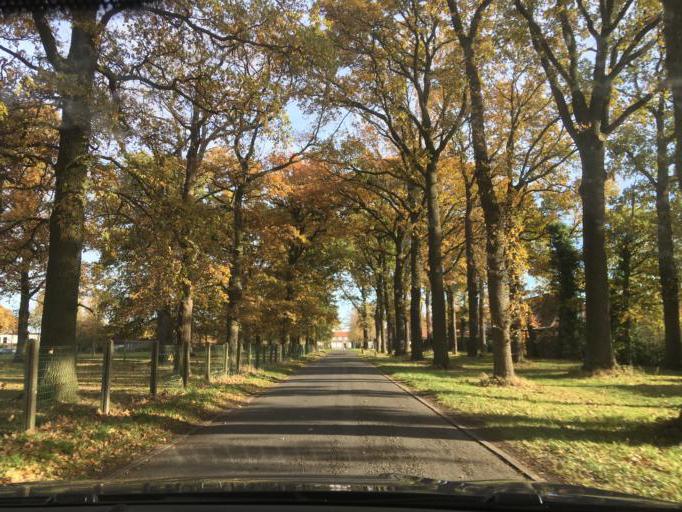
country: BE
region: Flanders
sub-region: Provincie West-Vlaanderen
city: Pittem
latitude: 50.9633
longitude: 3.2399
